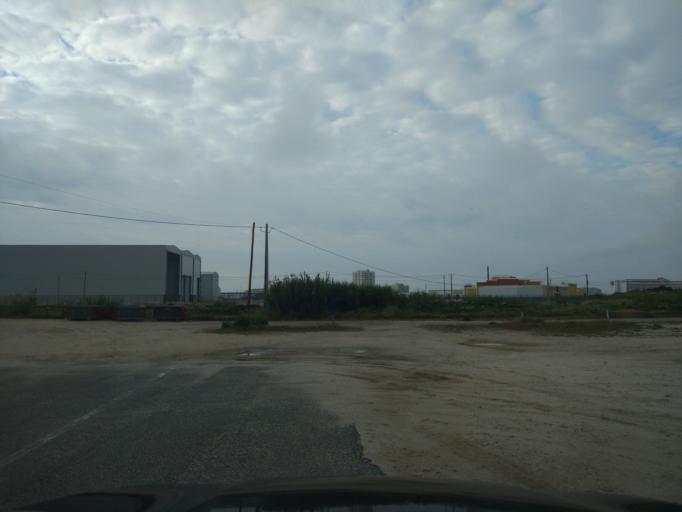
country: PT
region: Leiria
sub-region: Peniche
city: Peniche
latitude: 39.3506
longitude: -9.3653
